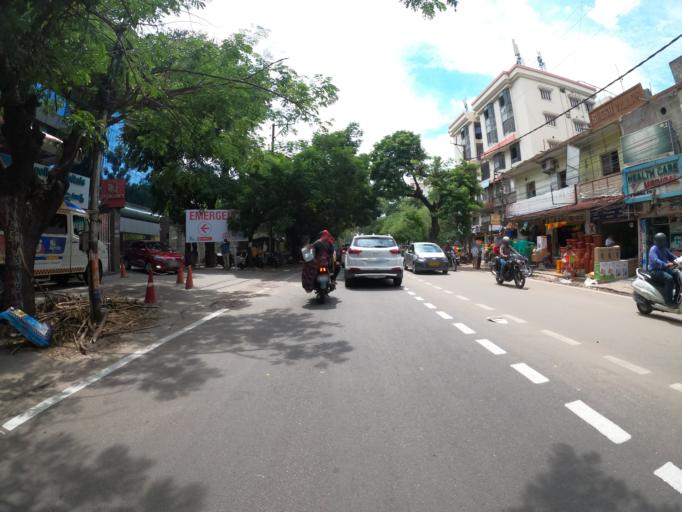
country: IN
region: Telangana
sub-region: Hyderabad
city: Hyderabad
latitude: 17.3996
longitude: 78.4794
